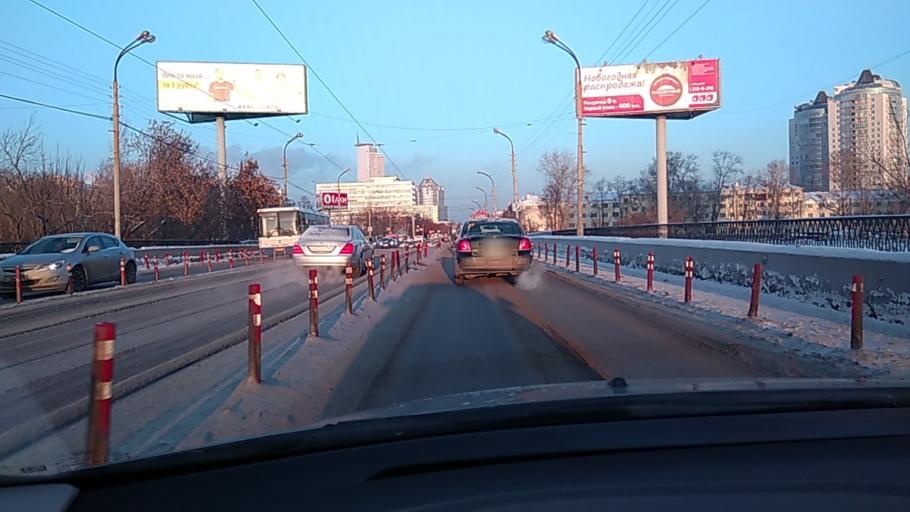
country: RU
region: Sverdlovsk
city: Yekaterinburg
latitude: 56.8485
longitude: 60.5904
